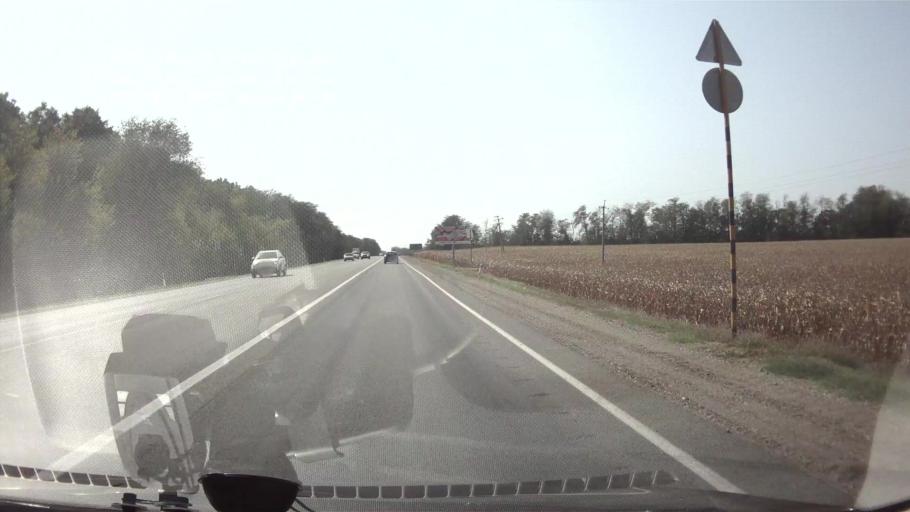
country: RU
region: Krasnodarskiy
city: Vasyurinskaya
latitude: 45.1512
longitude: 39.4437
